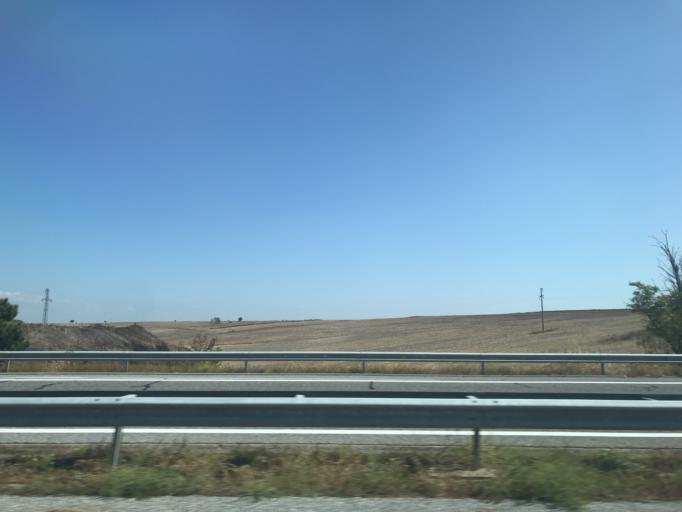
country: TR
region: Kirklareli
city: Luleburgaz
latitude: 41.4335
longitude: 27.3857
